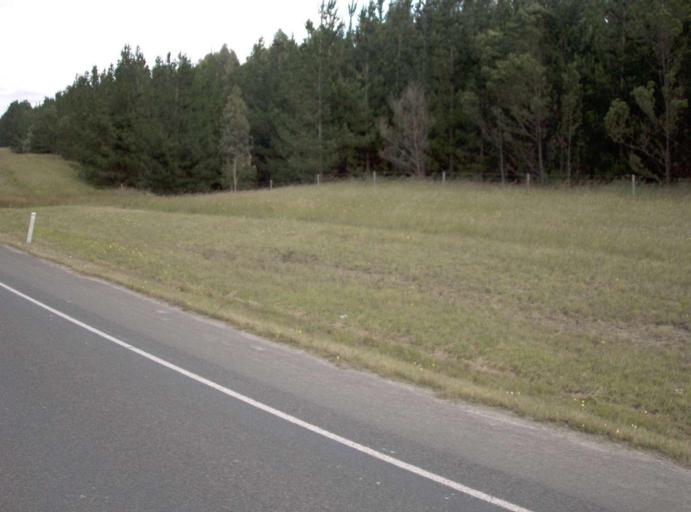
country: AU
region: Victoria
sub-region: Latrobe
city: Traralgon
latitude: -38.1876
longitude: 146.4695
